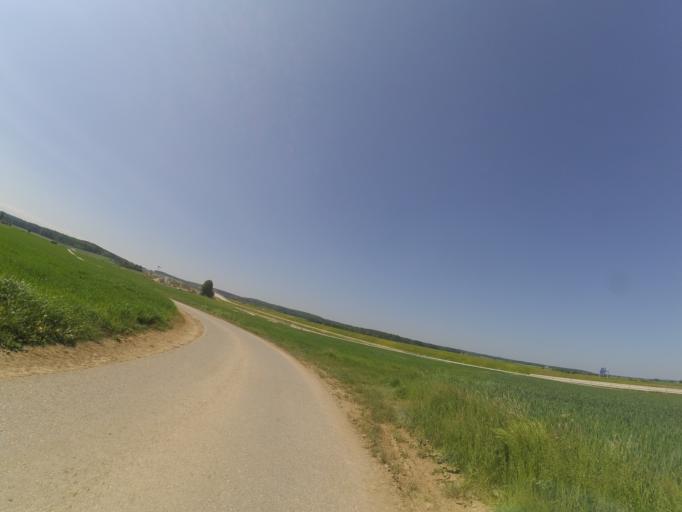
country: DE
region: Baden-Wuerttemberg
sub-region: Tuebingen Region
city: Merklingen
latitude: 48.5167
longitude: 9.7520
